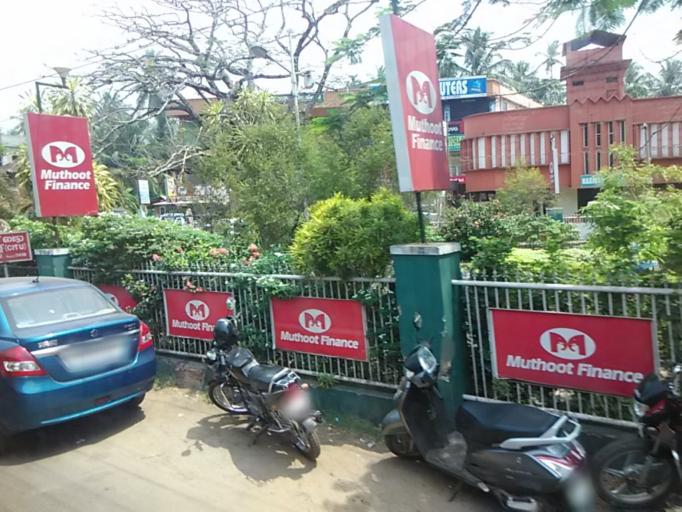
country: IN
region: Kerala
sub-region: Kozhikode
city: Kozhikode
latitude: 11.2689
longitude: 75.7766
